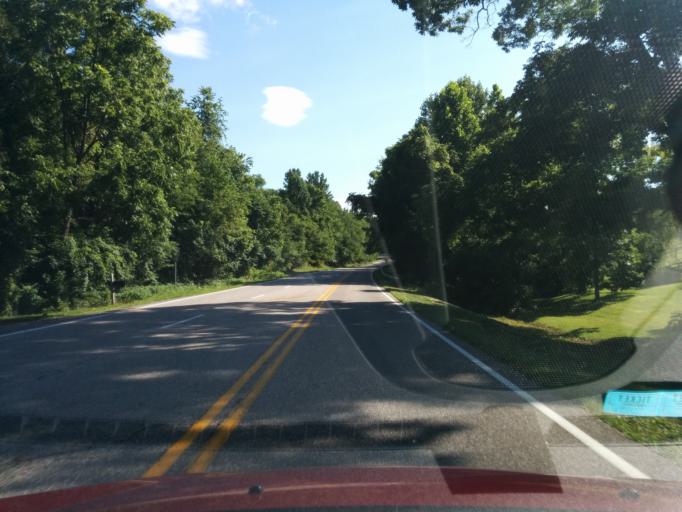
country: US
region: Virginia
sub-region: Rockbridge County
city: Glasgow
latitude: 37.7022
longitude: -79.4693
